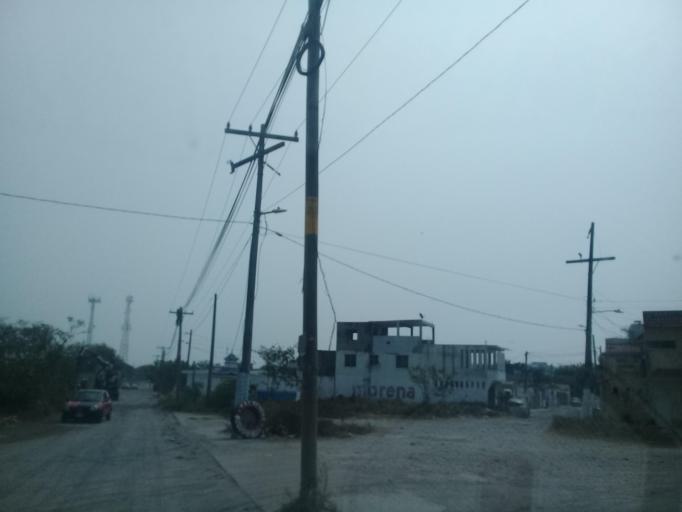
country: MX
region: Veracruz
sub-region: Veracruz
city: Fraccionamiento Costa Dorada
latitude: 19.2100
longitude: -96.2212
